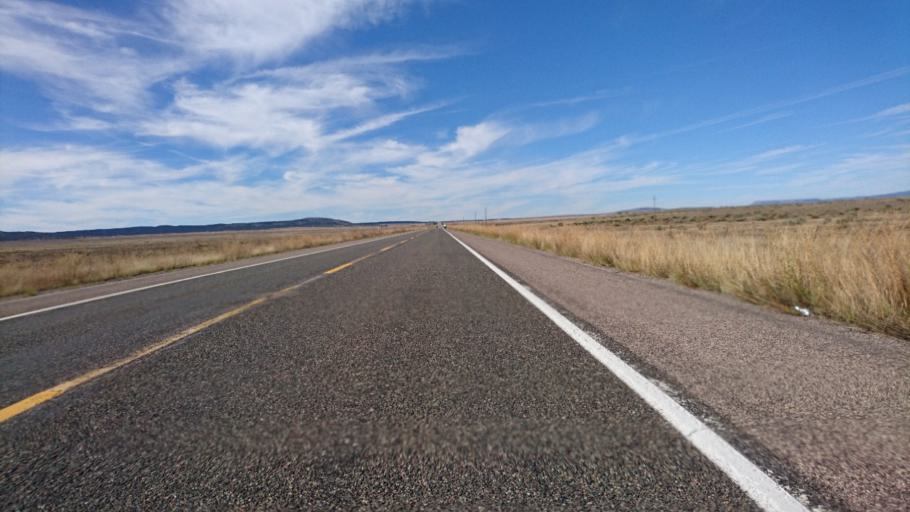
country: US
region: Arizona
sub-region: Mohave County
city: Peach Springs
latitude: 35.4586
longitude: -113.1068
